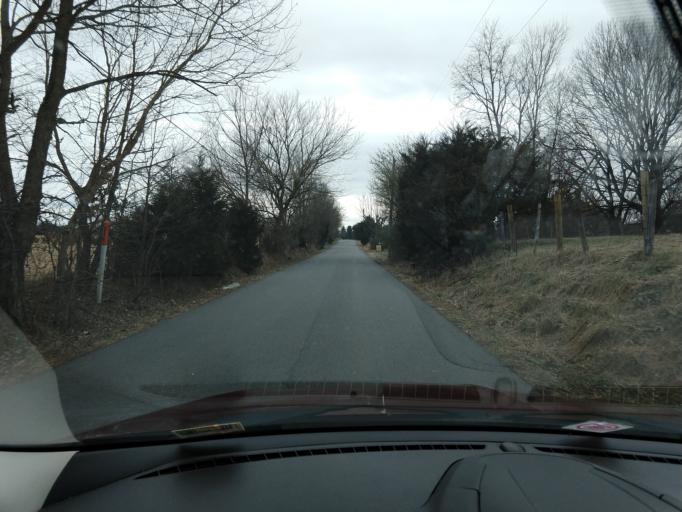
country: US
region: Virginia
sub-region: Rockingham County
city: Grottoes
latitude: 38.2508
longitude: -78.8655
